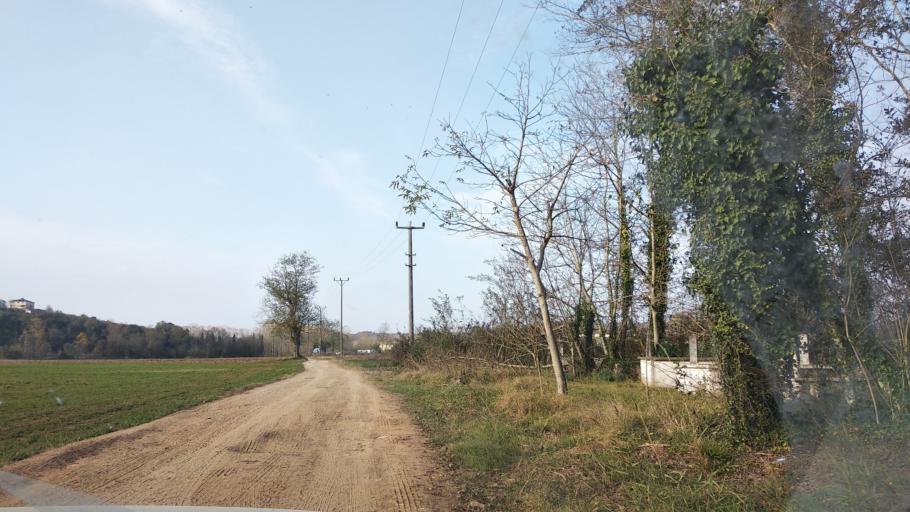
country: TR
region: Sakarya
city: Karasu
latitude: 41.0890
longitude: 30.5969
